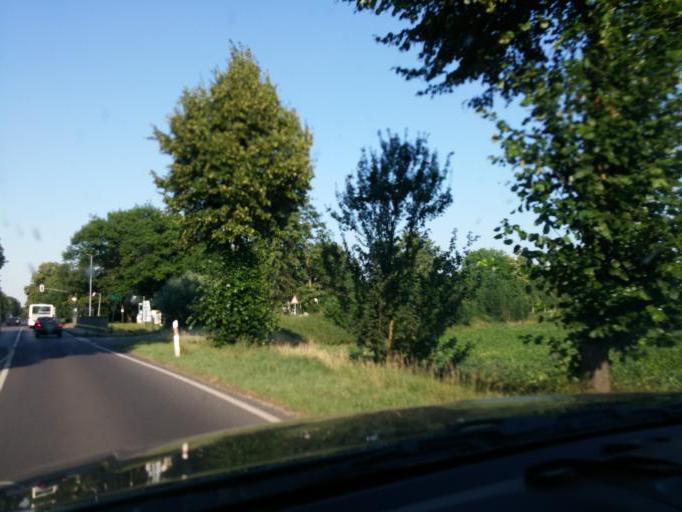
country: DE
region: North Rhine-Westphalia
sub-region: Regierungsbezirk Dusseldorf
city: Viersen
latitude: 51.2619
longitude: 6.4331
